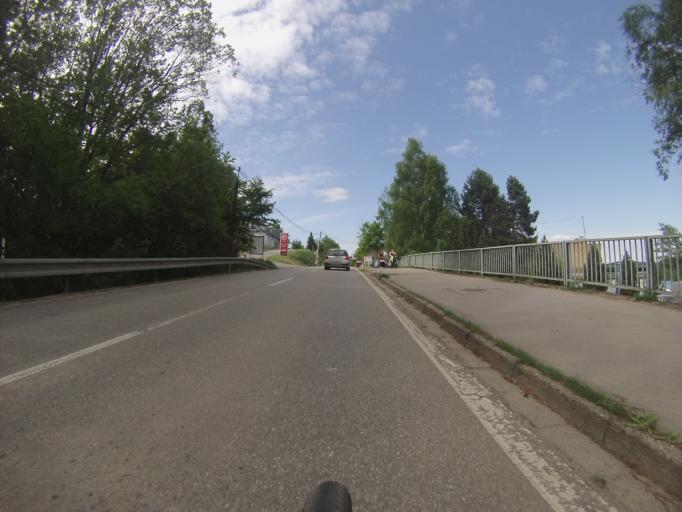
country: CZ
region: South Moravian
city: Troubsko
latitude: 49.2304
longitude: 16.5093
